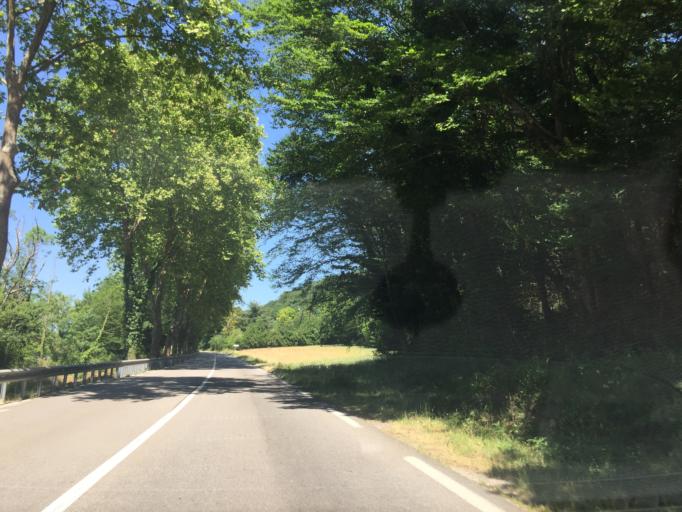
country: FR
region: Rhone-Alpes
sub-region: Departement de la Drome
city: Saint-Paul-les-Romans
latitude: 45.0377
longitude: 5.1267
